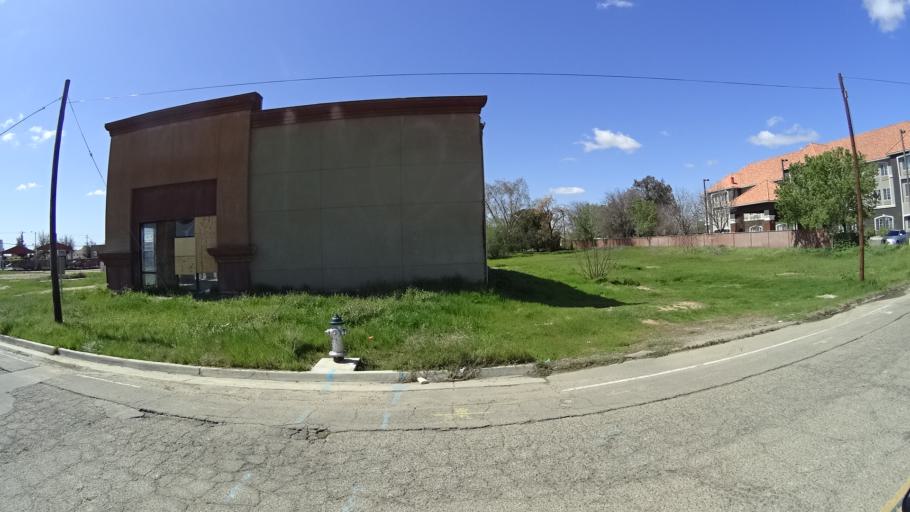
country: US
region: California
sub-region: Fresno County
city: West Park
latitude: 36.8093
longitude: -119.8806
